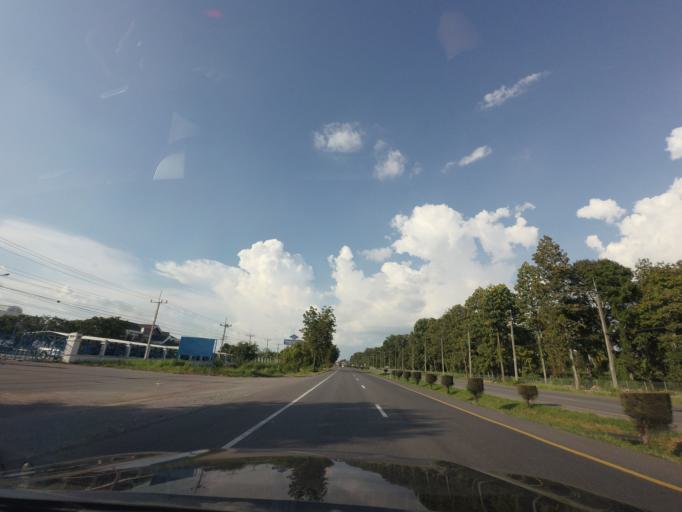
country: TH
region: Khon Kaen
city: Ban Haet
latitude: 16.1370
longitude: 102.7474
